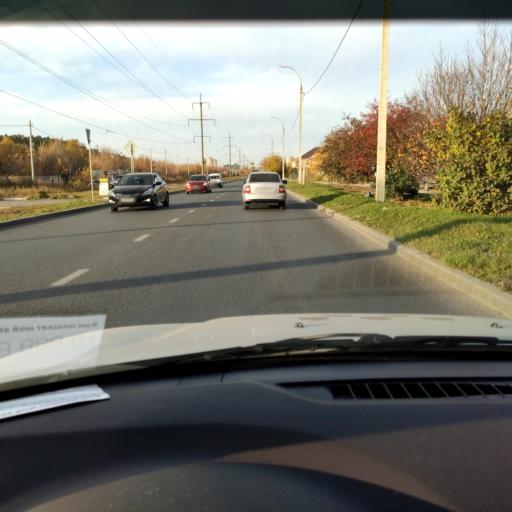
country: RU
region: Samara
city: Tol'yatti
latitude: 53.5161
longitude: 49.3957
